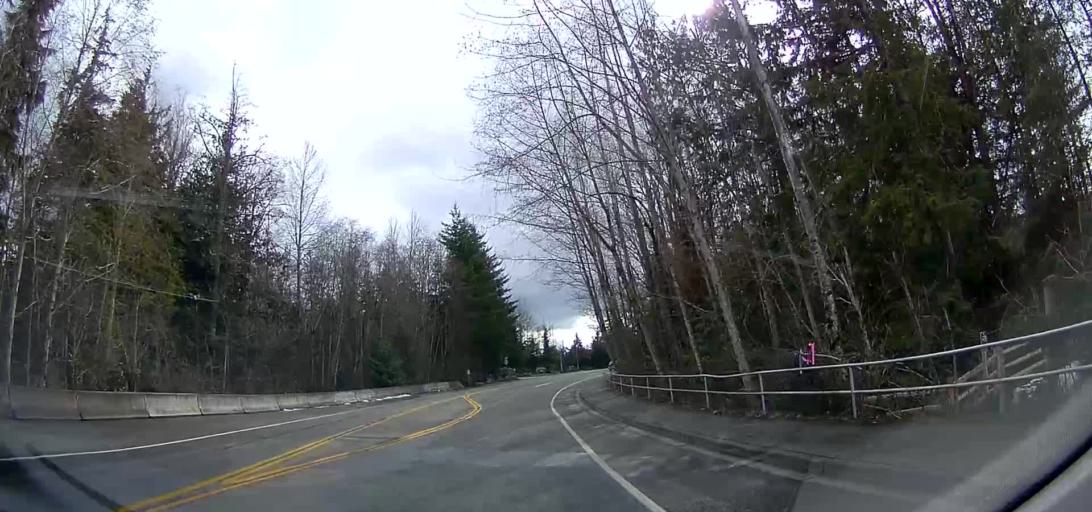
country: US
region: Washington
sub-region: Skagit County
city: Big Lake
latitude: 48.4142
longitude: -122.2865
